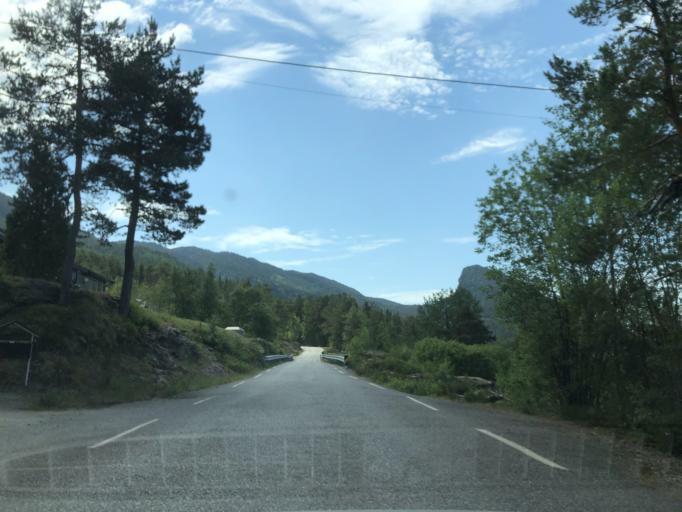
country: NO
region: Hordaland
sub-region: Jondal
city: Jondal
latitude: 60.3095
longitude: 6.2985
